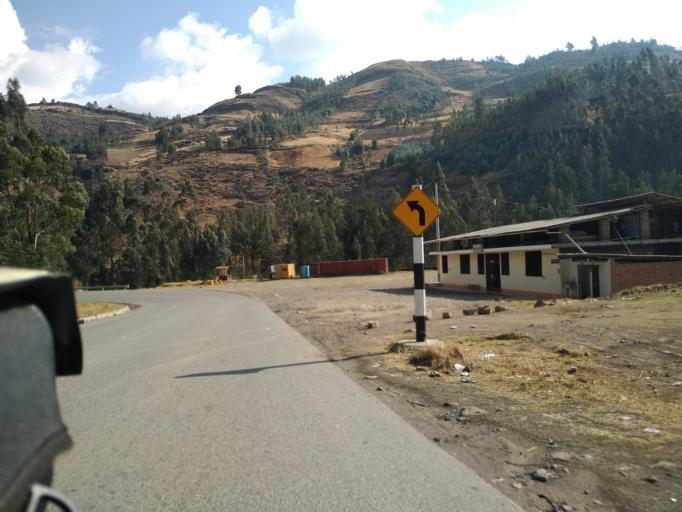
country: PE
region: La Libertad
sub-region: Provincia de Otuzco
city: Mache
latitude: -7.9975
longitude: -78.5069
